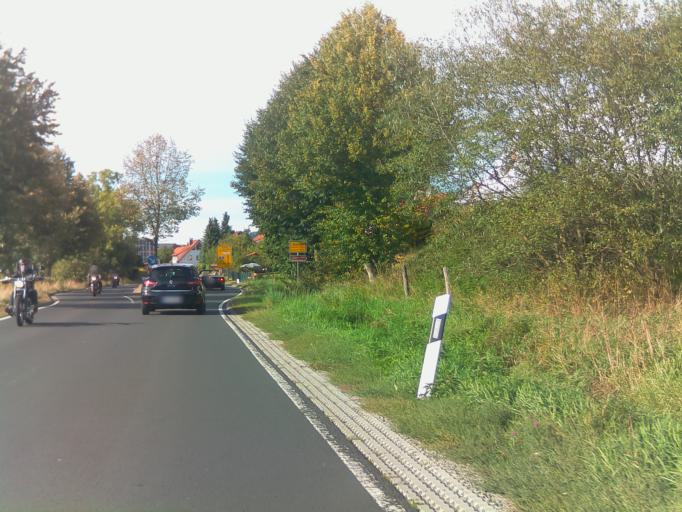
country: DE
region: Hesse
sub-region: Regierungsbezirk Kassel
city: Hilders
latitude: 50.5521
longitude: 10.0116
